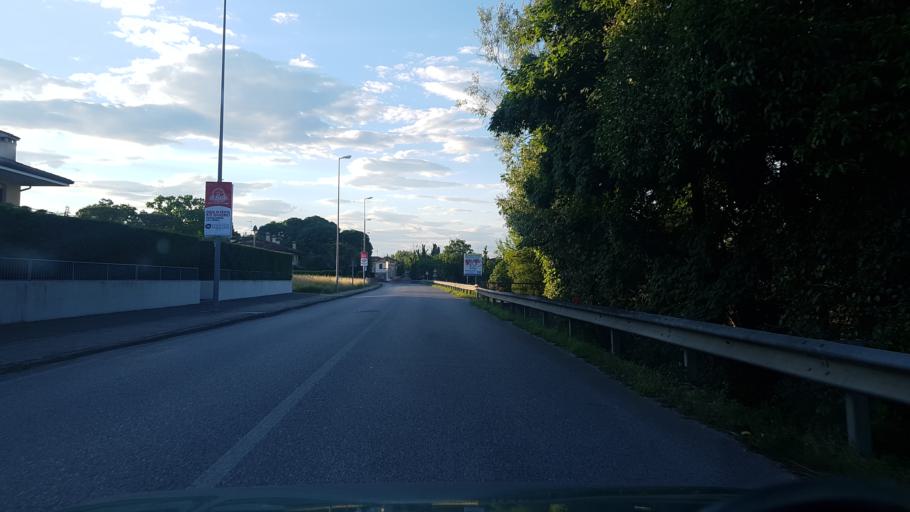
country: IT
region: Friuli Venezia Giulia
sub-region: Provincia di Udine
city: Santa Maria la Longa
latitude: 45.9307
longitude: 13.2925
